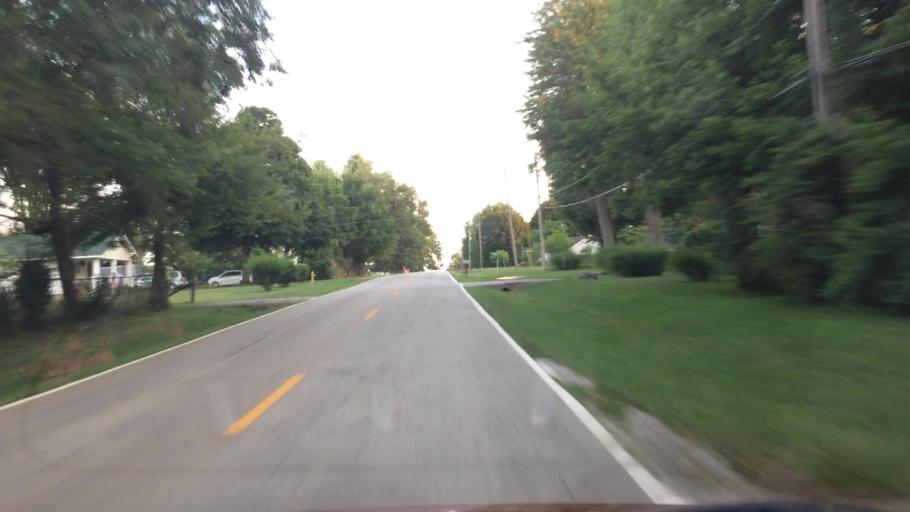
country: US
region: Missouri
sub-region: Greene County
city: Springfield
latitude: 37.2087
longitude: -93.3741
